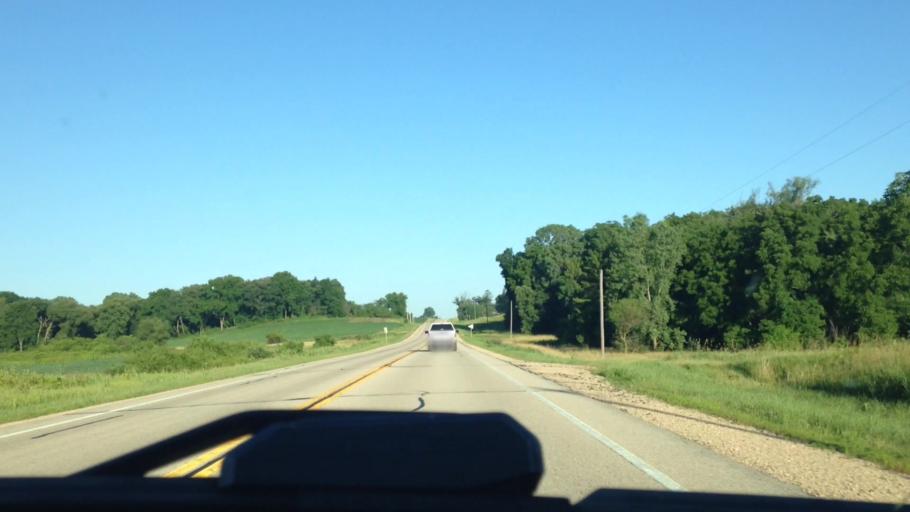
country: US
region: Wisconsin
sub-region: Columbia County
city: Rio
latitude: 43.3405
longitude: -89.1765
